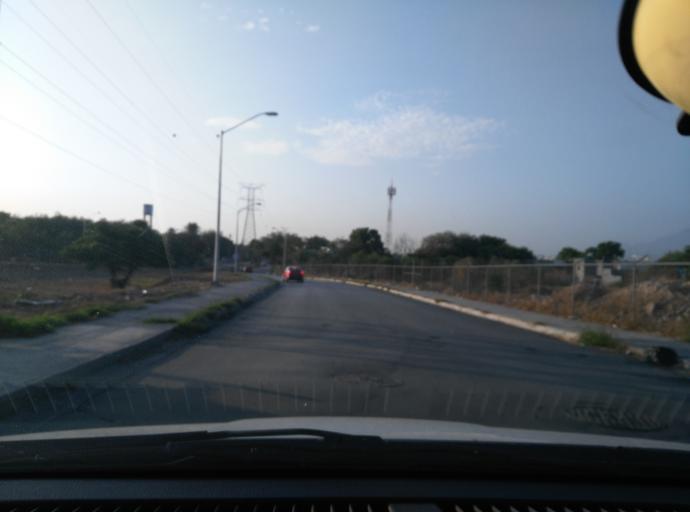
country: MX
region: Nuevo Leon
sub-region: San Nicolas de los Garza
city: San Nicolas de los Garza
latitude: 25.7592
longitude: -100.2514
